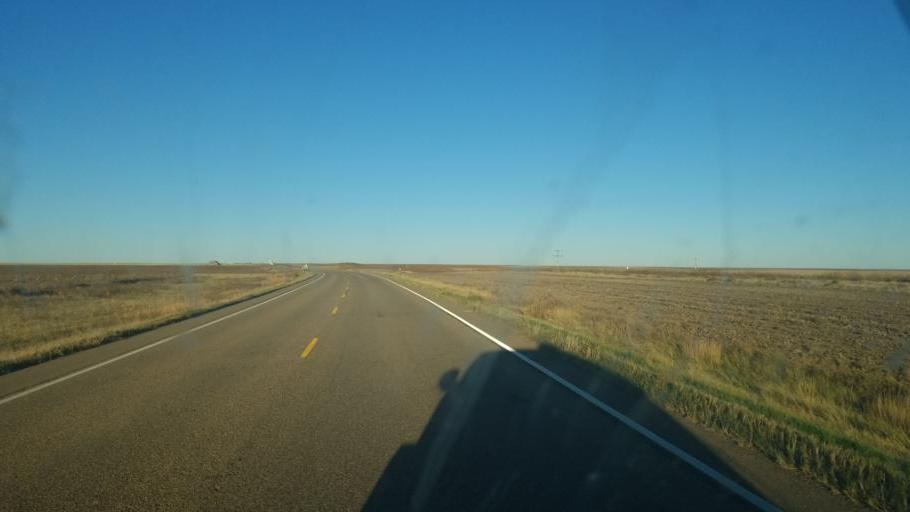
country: US
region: Colorado
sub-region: Cheyenne County
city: Cheyenne Wells
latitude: 38.8172
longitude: -102.4918
